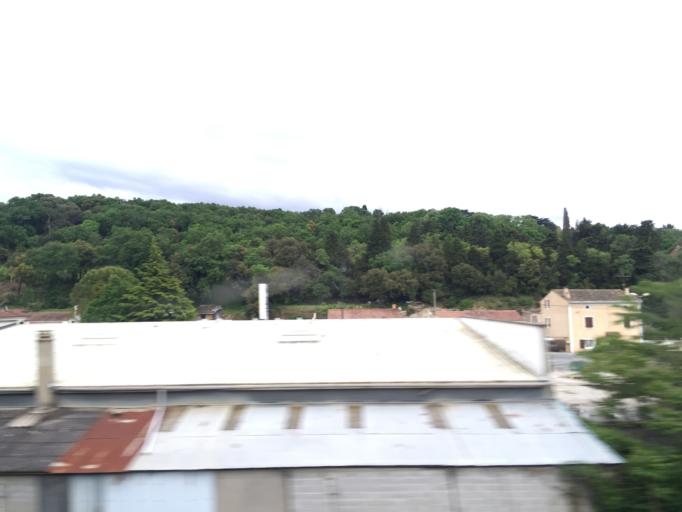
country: FR
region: Rhone-Alpes
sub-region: Departement de la Drome
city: Ancone
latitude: 44.5902
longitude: 4.7507
